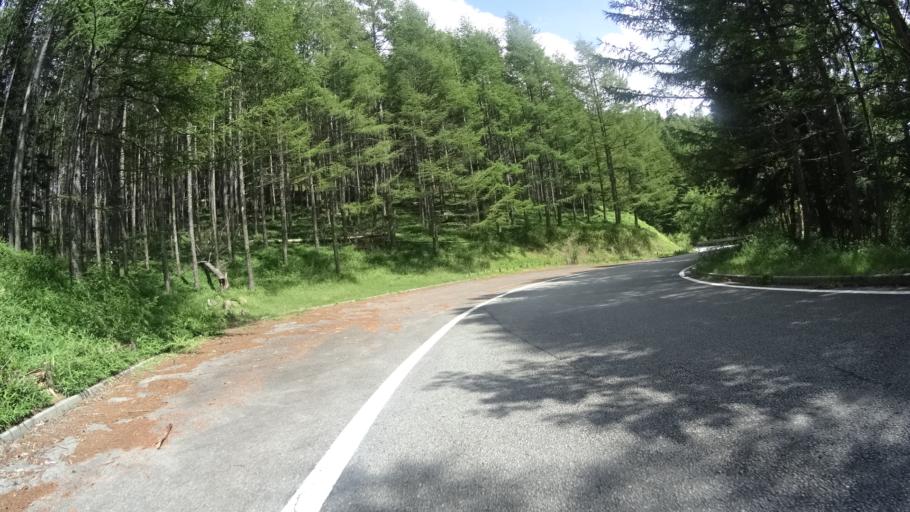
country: JP
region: Yamanashi
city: Enzan
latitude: 35.8504
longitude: 138.6414
